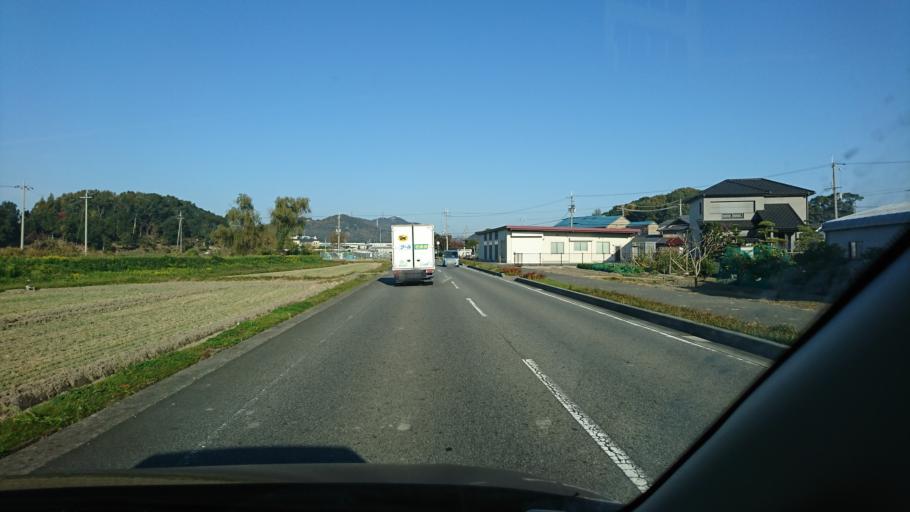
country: JP
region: Hyogo
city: Kakogawacho-honmachi
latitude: 34.7828
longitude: 134.8720
